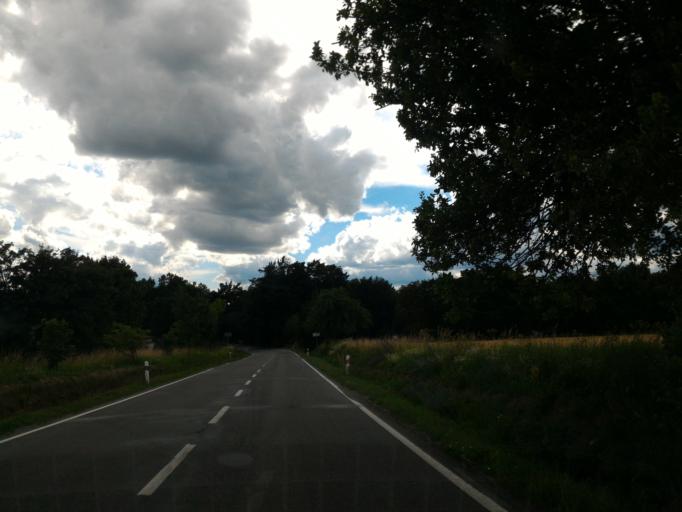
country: CZ
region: Vysocina
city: Bohdalov
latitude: 49.4590
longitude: 15.8092
